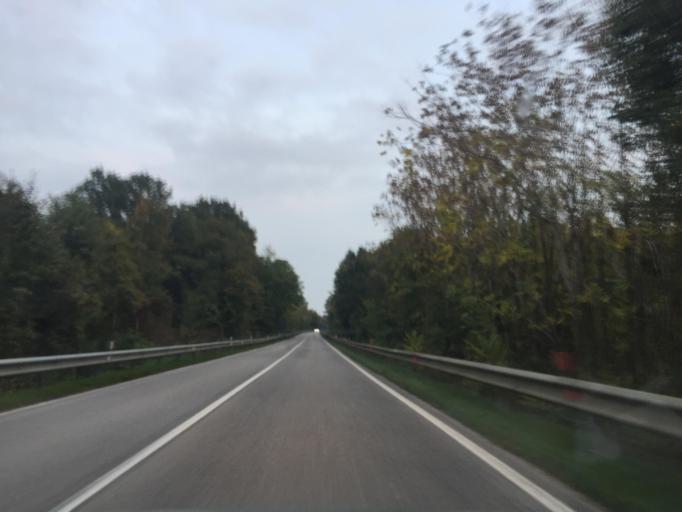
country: IT
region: Friuli Venezia Giulia
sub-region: Provincia di Pordenone
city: Fanna
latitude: 46.1698
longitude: 12.7556
